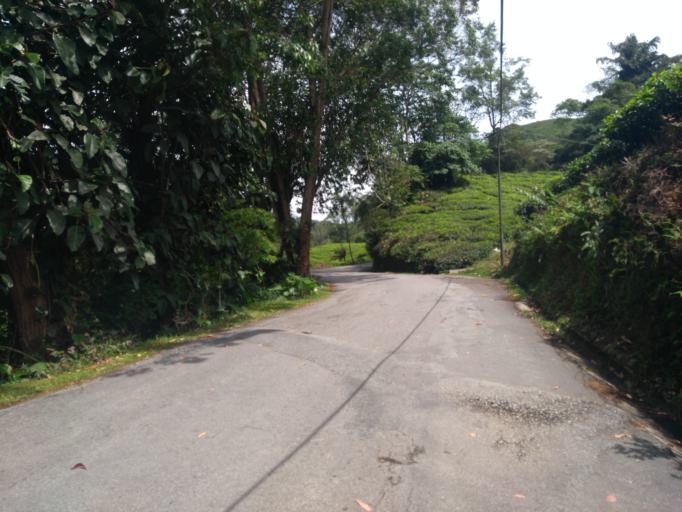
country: MY
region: Pahang
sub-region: Cameron Highlands
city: Tanah Rata
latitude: 4.5187
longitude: 101.4077
